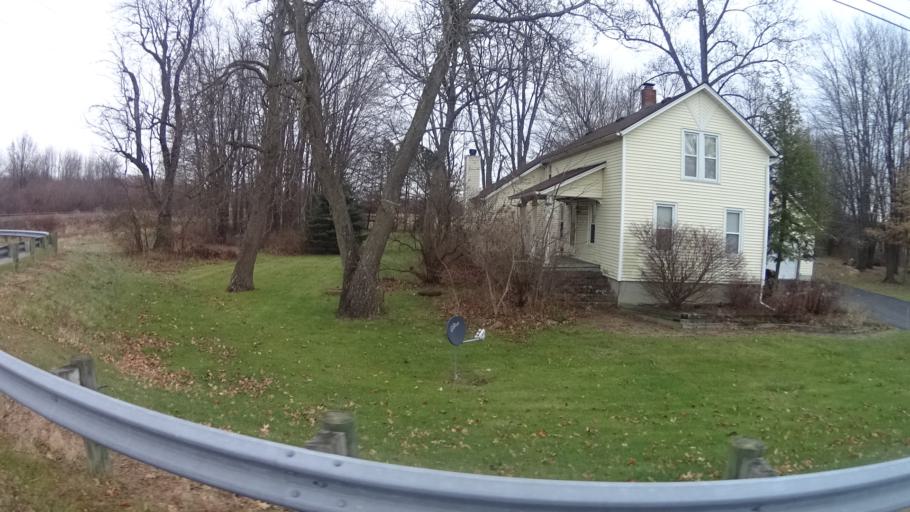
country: US
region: Ohio
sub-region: Lorain County
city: North Ridgeville
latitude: 41.3748
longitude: -82.0188
